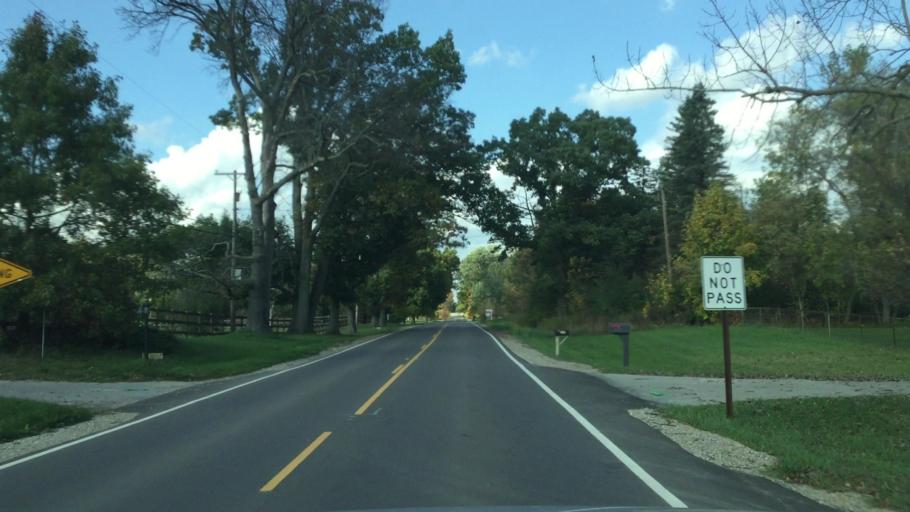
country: US
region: Michigan
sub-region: Genesee County
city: Fenton
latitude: 42.7104
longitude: -83.7035
